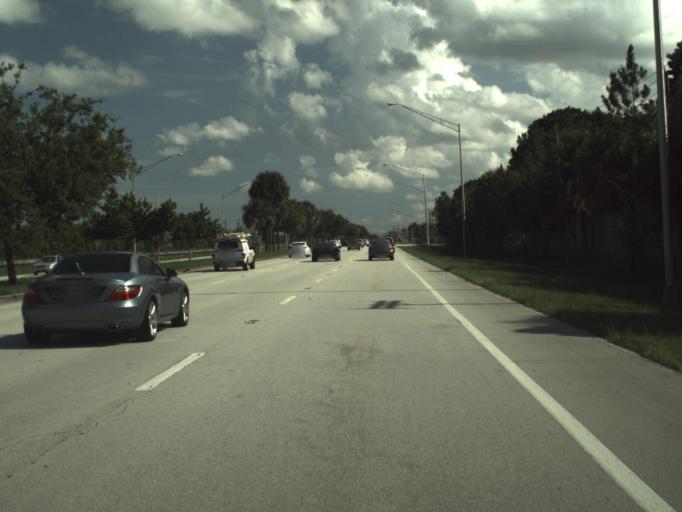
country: US
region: Florida
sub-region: Palm Beach County
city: Boca Pointe
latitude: 26.3764
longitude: -80.2037
